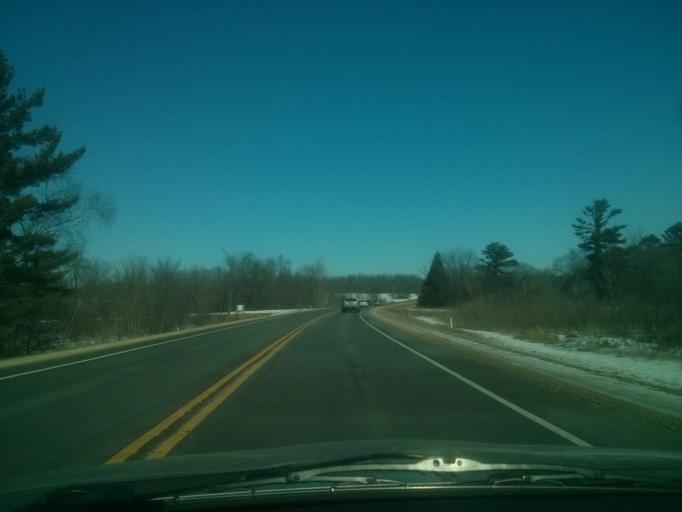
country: US
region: Wisconsin
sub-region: Polk County
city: Clear Lake
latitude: 45.1732
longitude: -92.2838
